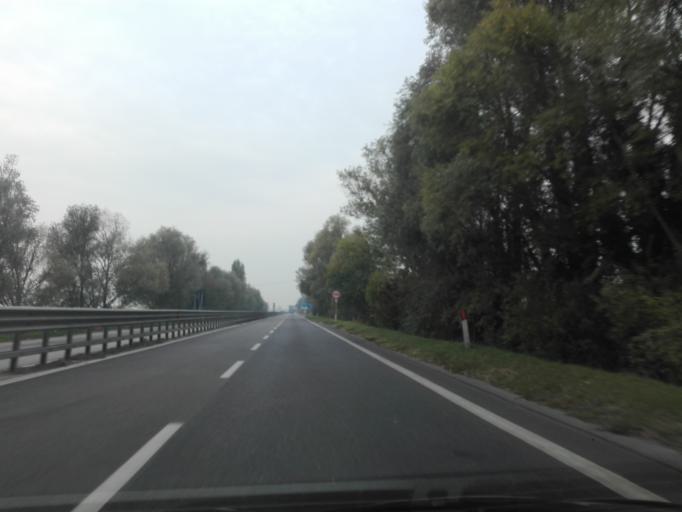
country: IT
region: Veneto
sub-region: Provincia di Rovigo
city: San Bellino
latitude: 45.0259
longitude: 11.5840
